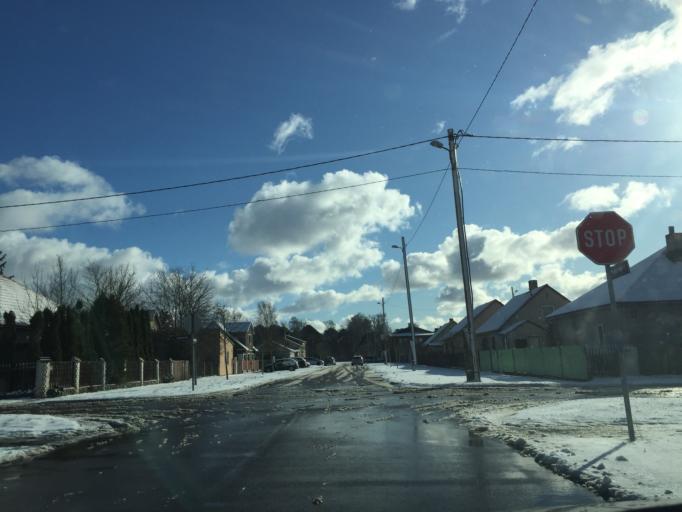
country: LV
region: Ventspils
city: Ventspils
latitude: 57.3806
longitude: 21.5550
